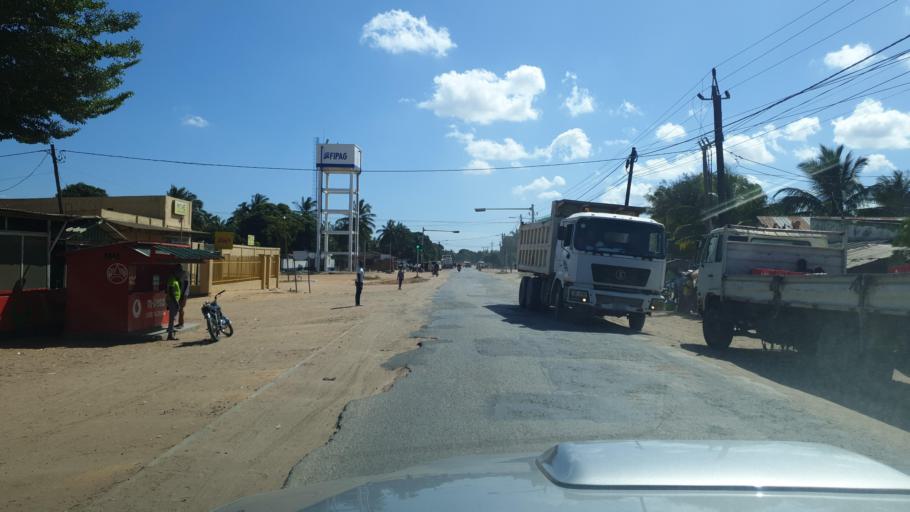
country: MZ
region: Nampula
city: Nacala
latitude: -14.5222
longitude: 40.6953
